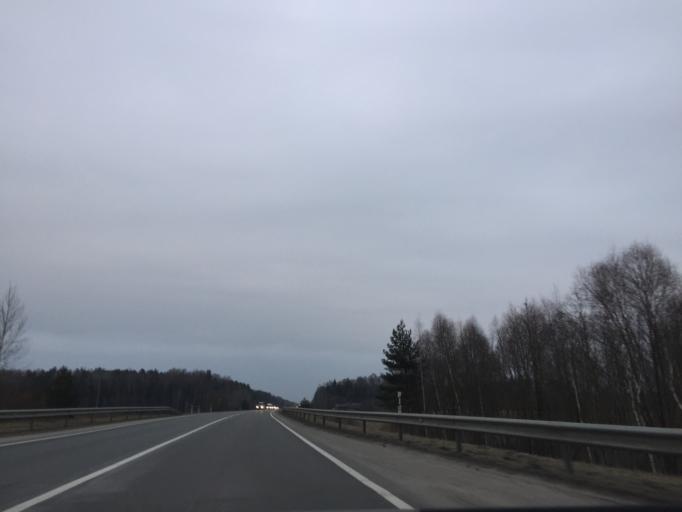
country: LV
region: Ozolnieku
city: Ozolnieki
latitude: 56.6910
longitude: 23.8228
